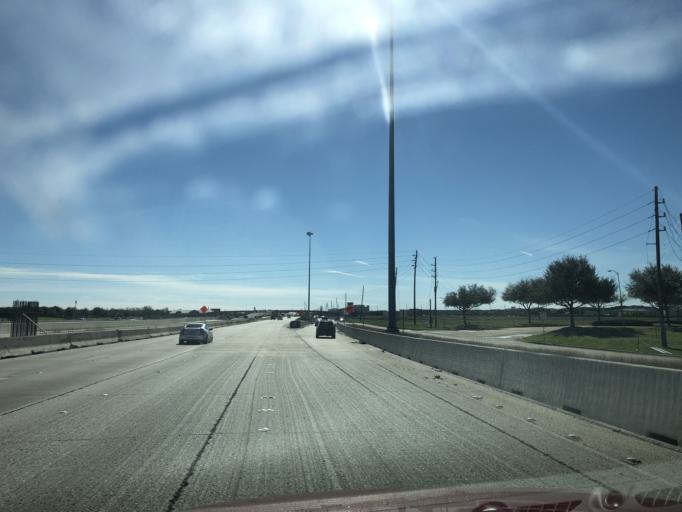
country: US
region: Texas
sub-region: Brazoria County
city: Brookside Village
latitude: 29.5768
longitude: -95.3864
